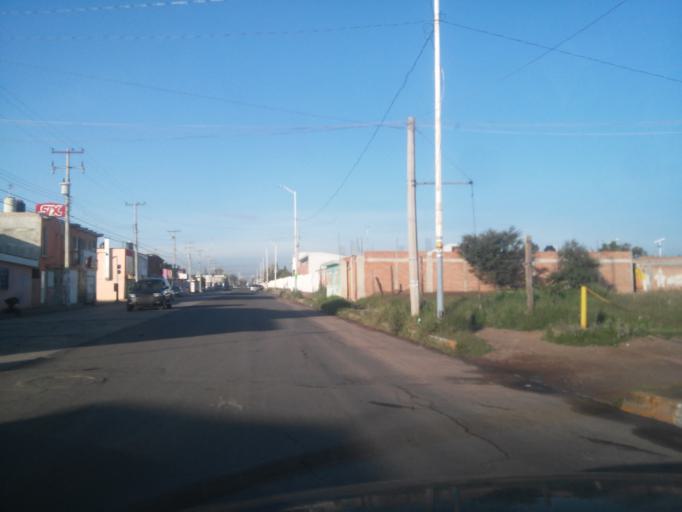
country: MX
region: Durango
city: Victoria de Durango
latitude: 24.0520
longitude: -104.6084
